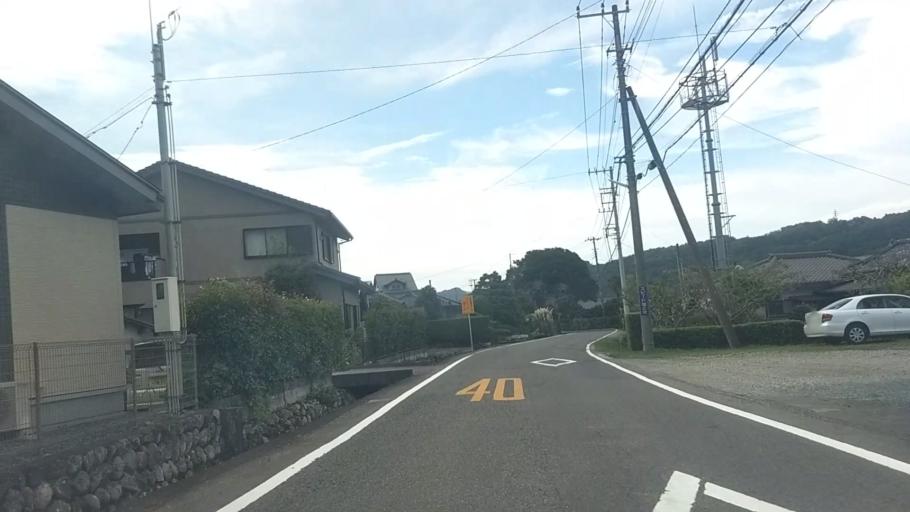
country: JP
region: Shizuoka
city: Ito
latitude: 34.9669
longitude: 138.9697
